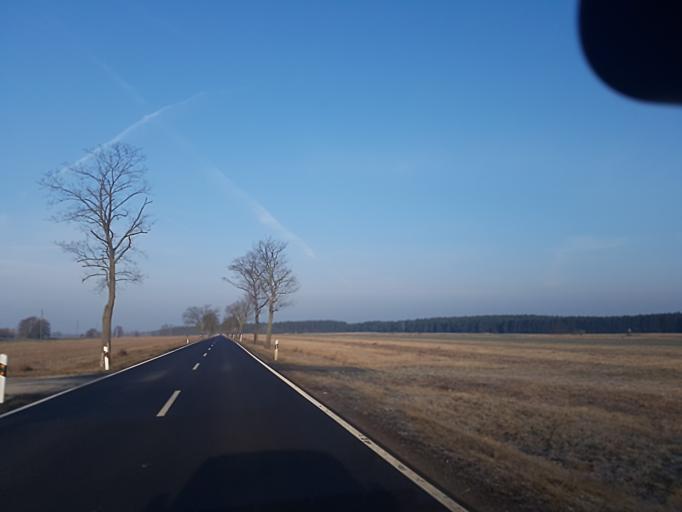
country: DE
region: Brandenburg
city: Golzow
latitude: 52.2643
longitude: 12.6557
